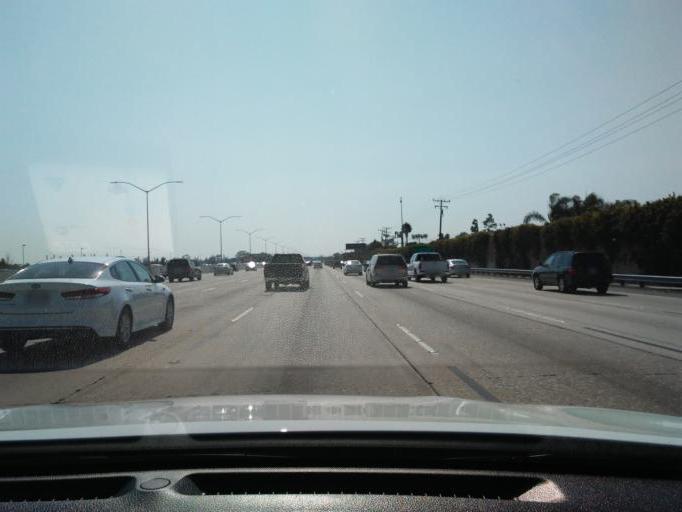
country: US
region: California
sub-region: Orange County
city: Rossmoor
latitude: 33.7745
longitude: -118.0598
